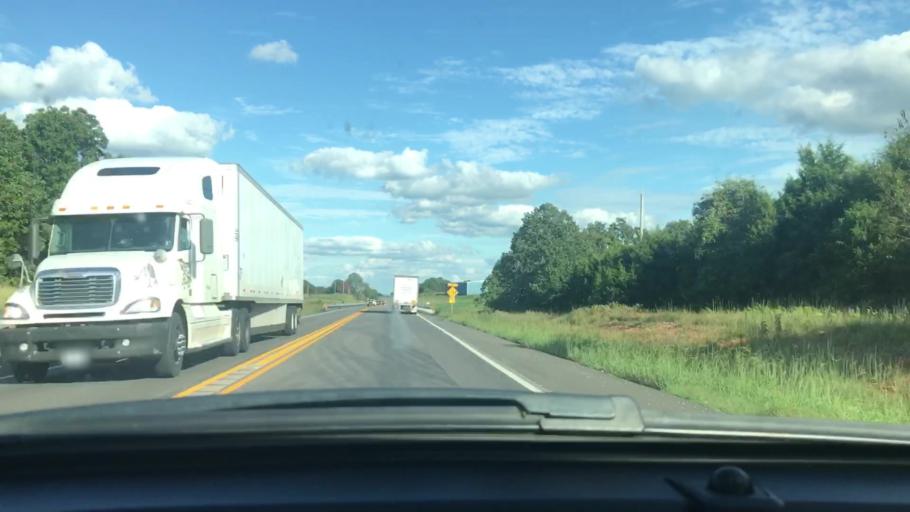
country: US
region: Missouri
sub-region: Oregon County
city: Thayer
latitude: 36.5886
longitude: -91.6376
